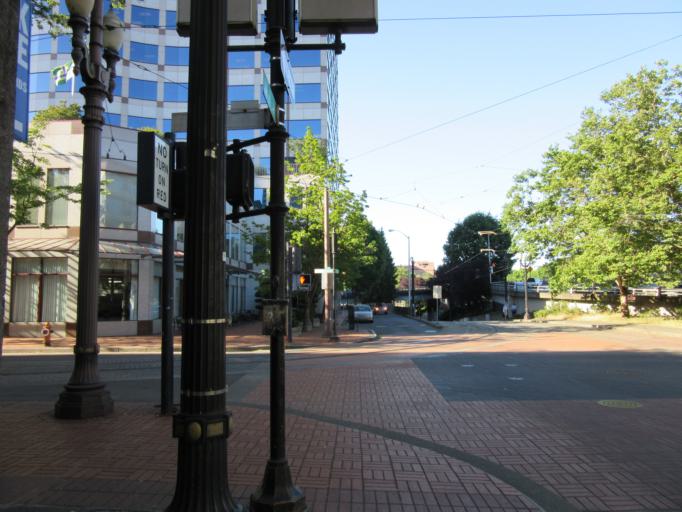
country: US
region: Oregon
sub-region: Multnomah County
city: Portland
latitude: 45.5177
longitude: -122.6737
